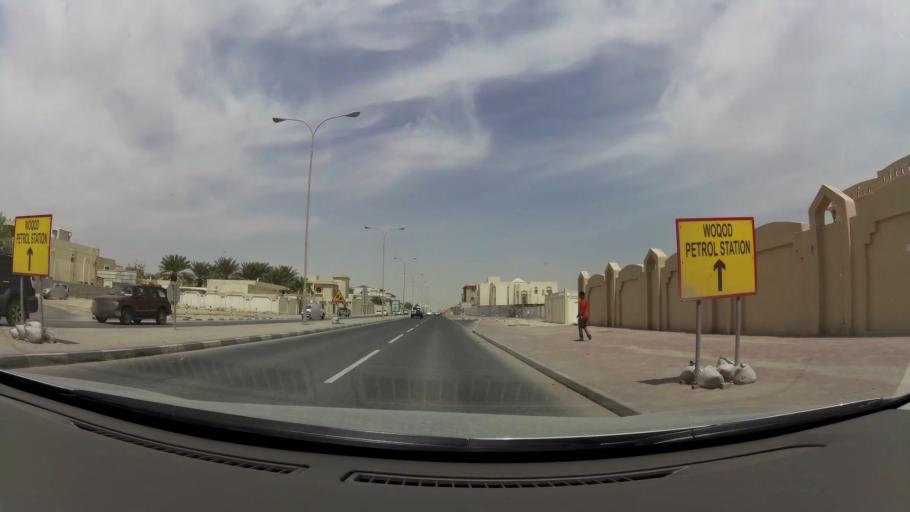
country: QA
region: Baladiyat ar Rayyan
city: Ar Rayyan
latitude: 25.3015
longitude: 51.4121
